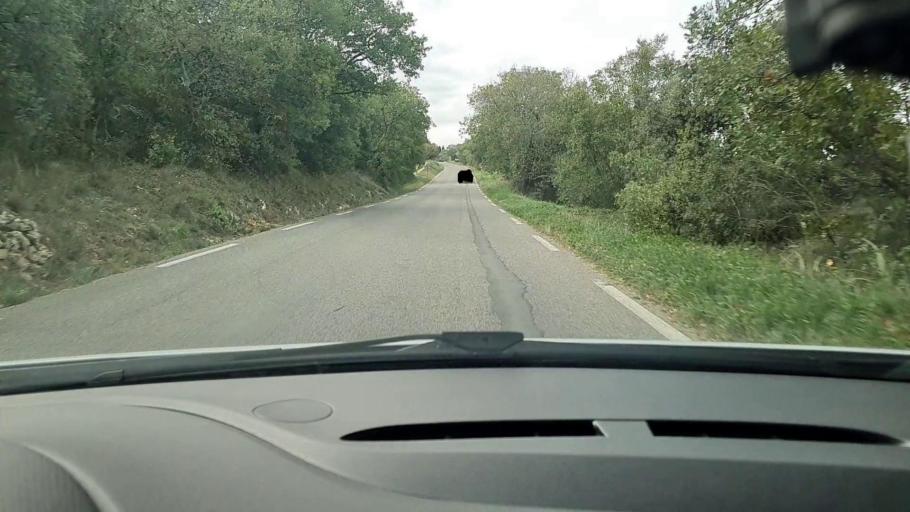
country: FR
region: Languedoc-Roussillon
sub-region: Departement du Gard
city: Salindres
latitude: 44.1701
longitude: 4.2387
